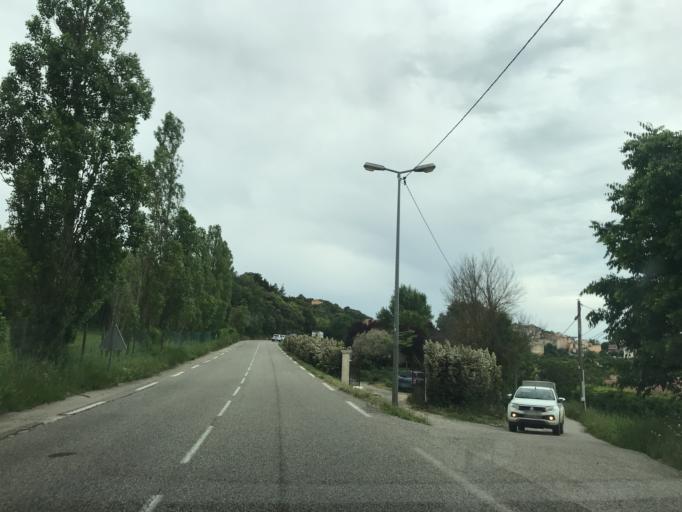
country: FR
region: Provence-Alpes-Cote d'Azur
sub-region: Departement du Var
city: Ginasservis
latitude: 43.6649
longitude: 5.8527
